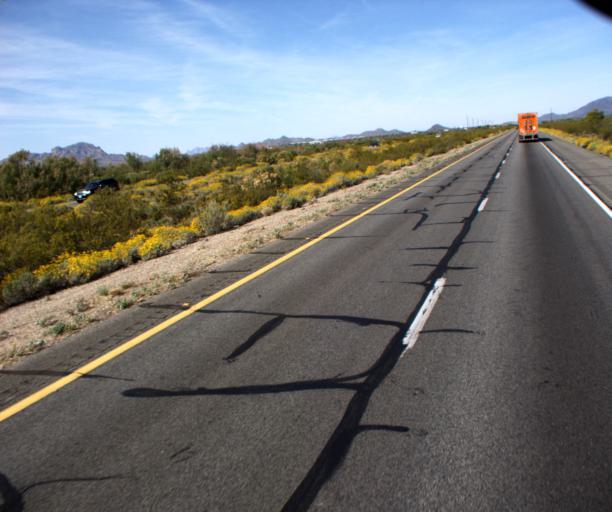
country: US
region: Arizona
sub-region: Maricopa County
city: Buckeye
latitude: 33.4911
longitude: -112.9079
